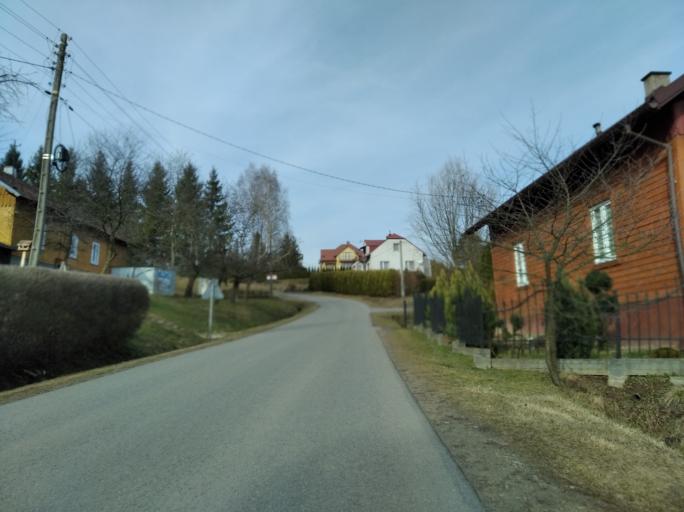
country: PL
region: Subcarpathian Voivodeship
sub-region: Powiat brzozowski
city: Turze Pole
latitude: 49.6682
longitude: 22.0033
